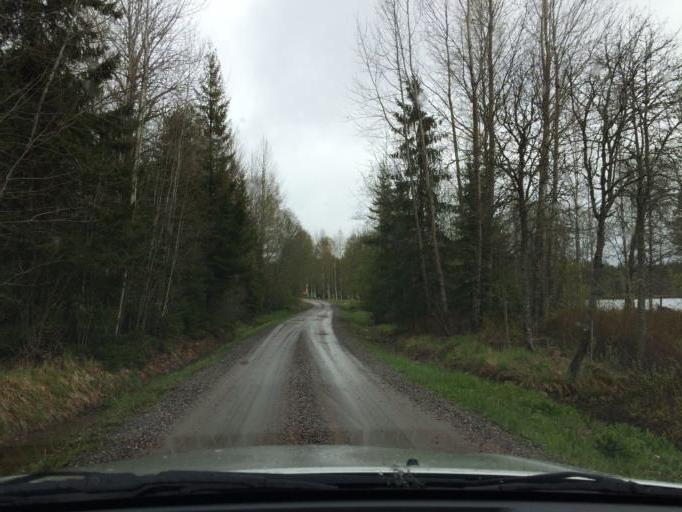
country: SE
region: Dalarna
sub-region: Ludvika Kommun
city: Abborrberget
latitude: 60.0219
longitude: 14.6265
